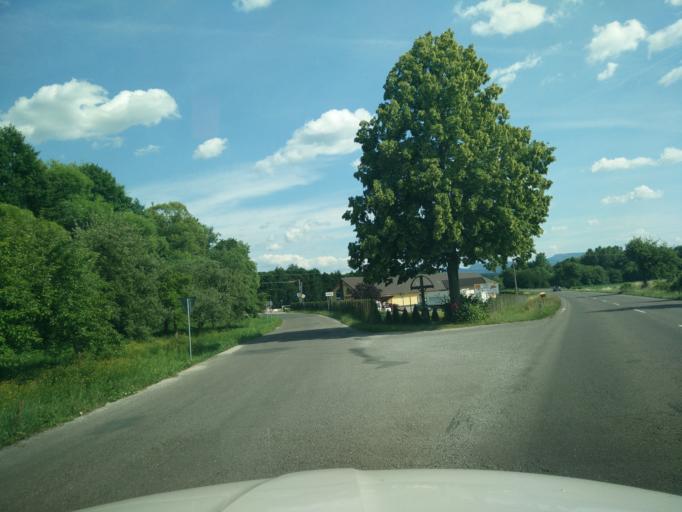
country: SK
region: Nitriansky
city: Prievidza
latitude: 48.8559
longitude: 18.6426
